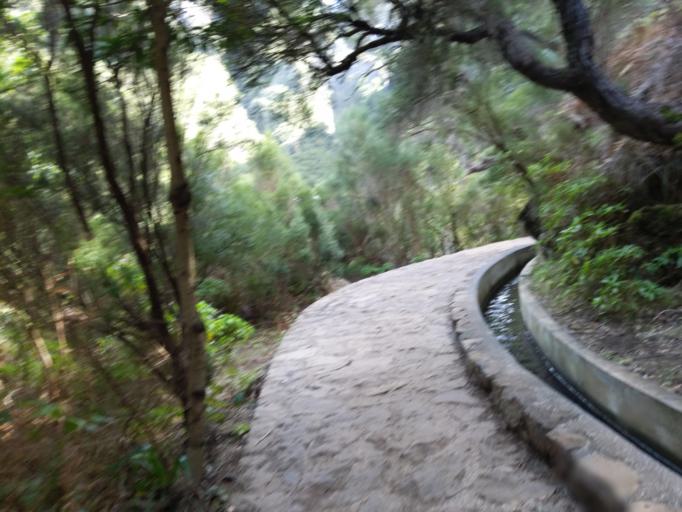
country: PT
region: Madeira
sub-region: Calheta
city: Arco da Calheta
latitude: 32.7624
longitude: -17.1277
